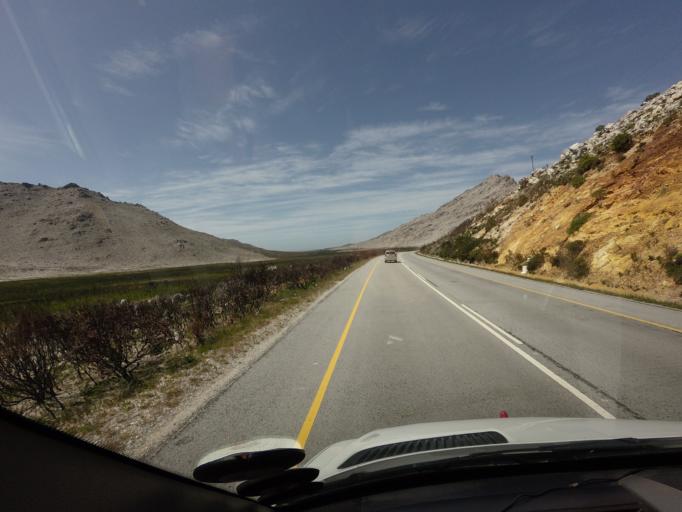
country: ZA
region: Western Cape
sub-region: Overberg District Municipality
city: Grabouw
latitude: -34.3187
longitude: 18.8317
